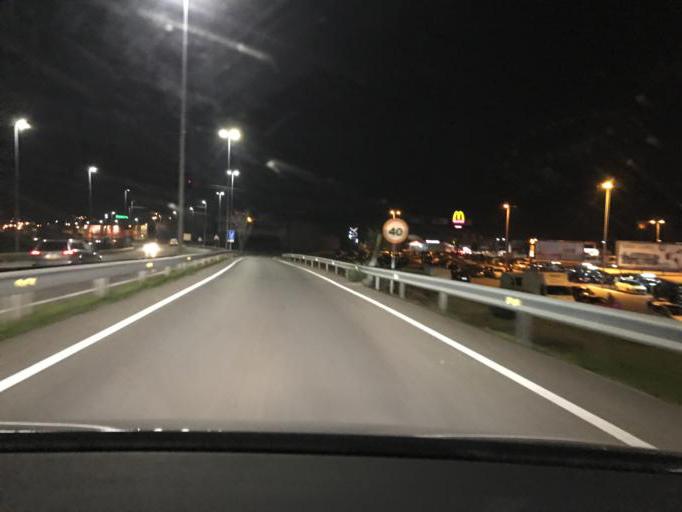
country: ES
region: Andalusia
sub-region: Provincia de Jaen
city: Jaen
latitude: 37.7822
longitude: -3.7660
